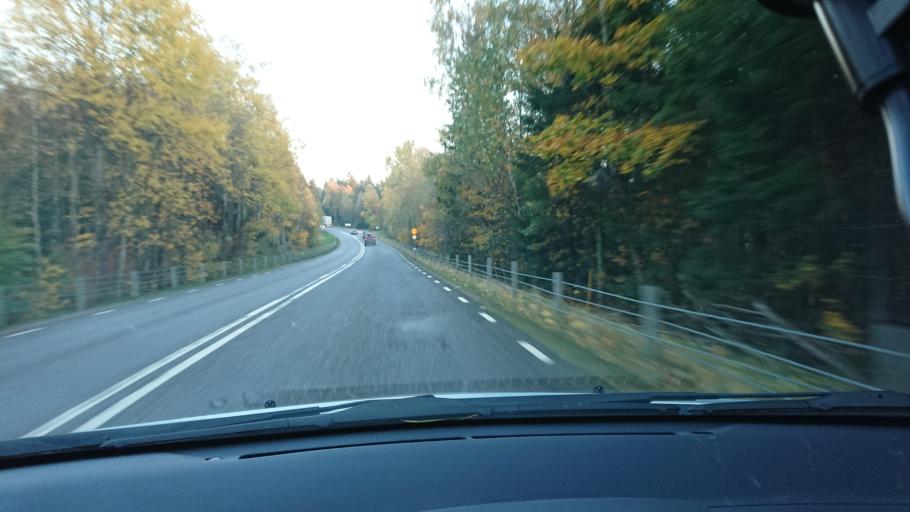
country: SE
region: Halland
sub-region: Laholms Kommun
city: Veinge
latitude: 56.7152
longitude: 13.1978
